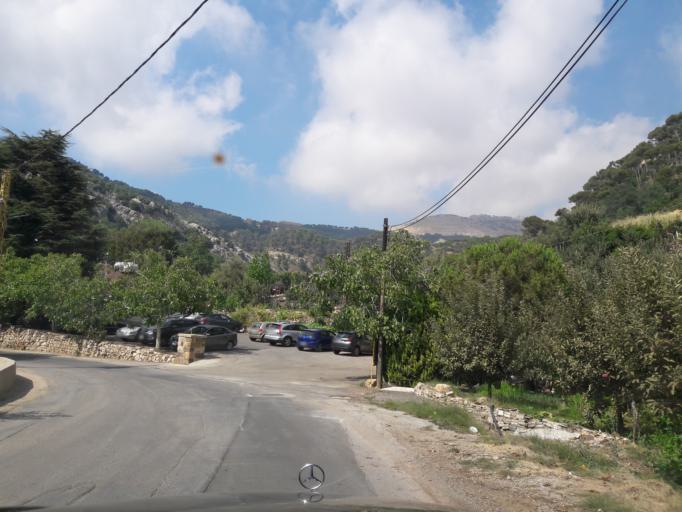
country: LB
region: Mont-Liban
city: Djounie
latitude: 33.9625
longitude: 35.7803
